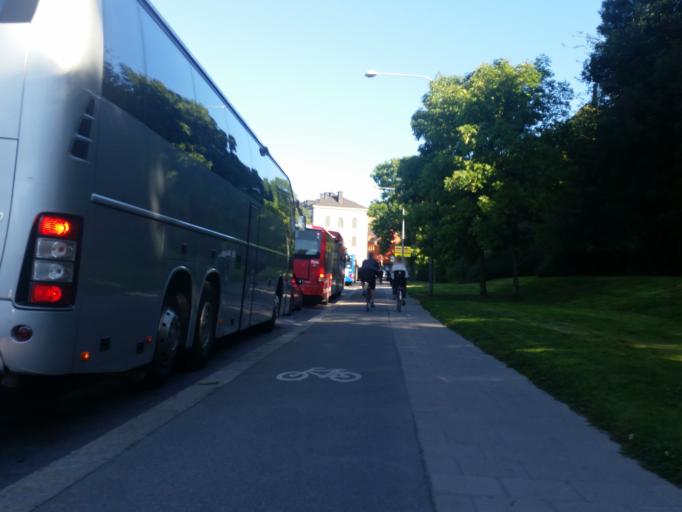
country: SE
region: Stockholm
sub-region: Stockholms Kommun
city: Stockholm
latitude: 59.3181
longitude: 18.0803
